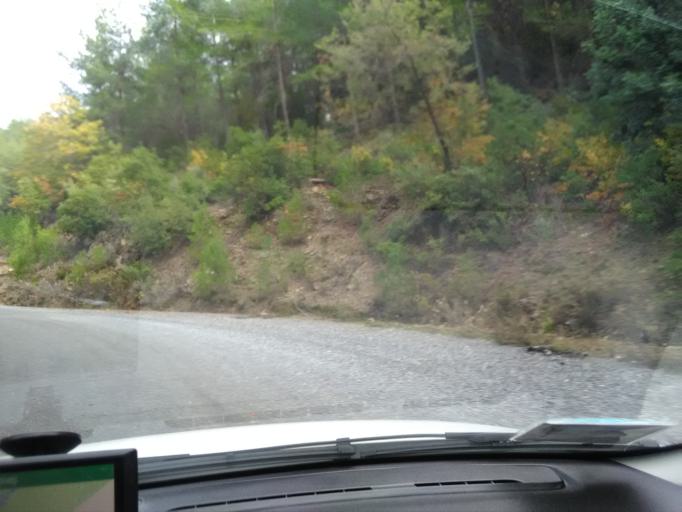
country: TR
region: Antalya
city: Gazipasa
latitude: 36.2465
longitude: 32.4210
